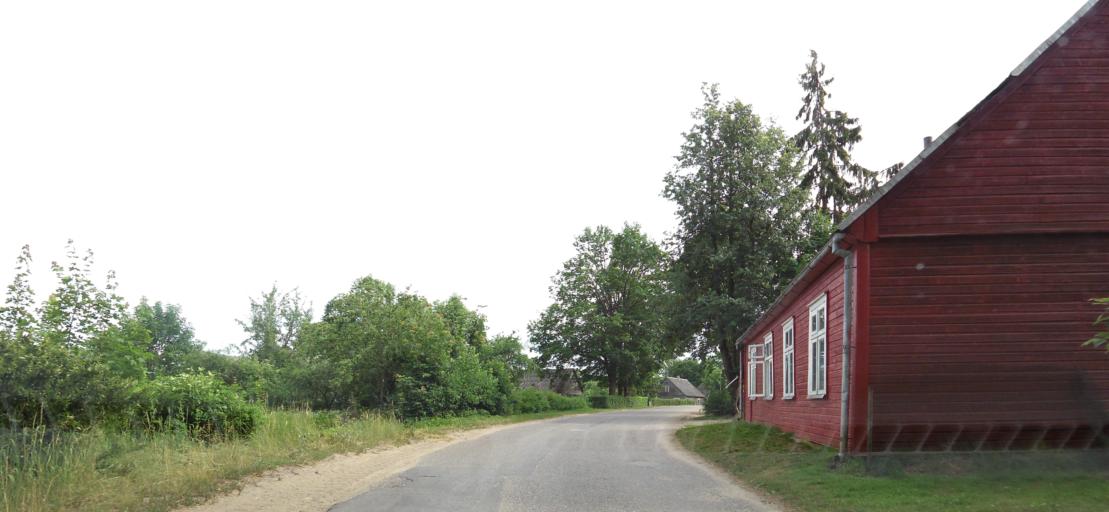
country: LV
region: Nereta
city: Nereta
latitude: 56.1504
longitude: 25.1396
